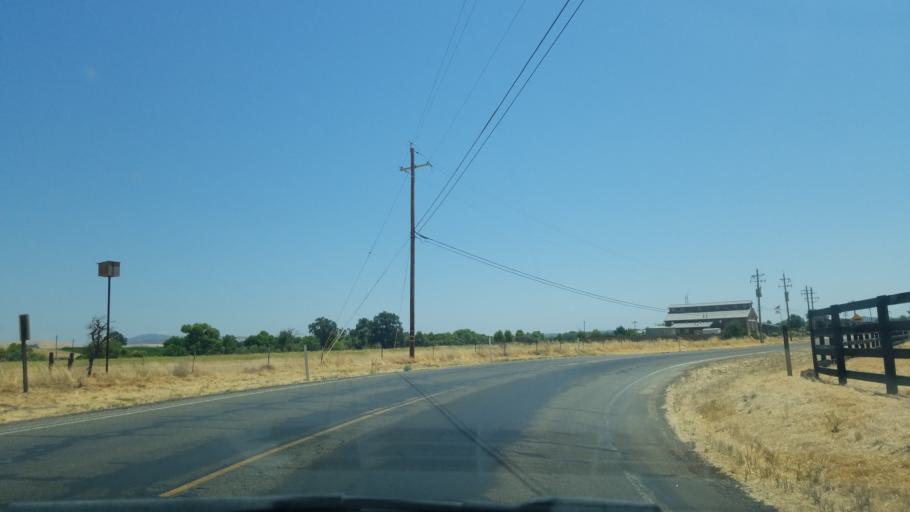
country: US
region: California
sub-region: San Luis Obispo County
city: Atascadero
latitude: 35.5284
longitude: -120.5215
